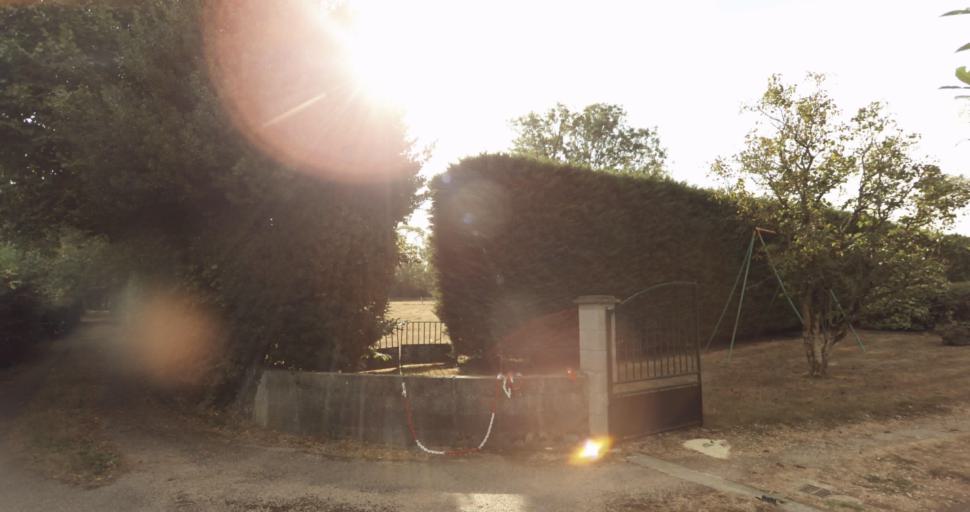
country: FR
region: Lower Normandy
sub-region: Departement de l'Orne
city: Vimoutiers
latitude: 48.9299
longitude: 0.2322
